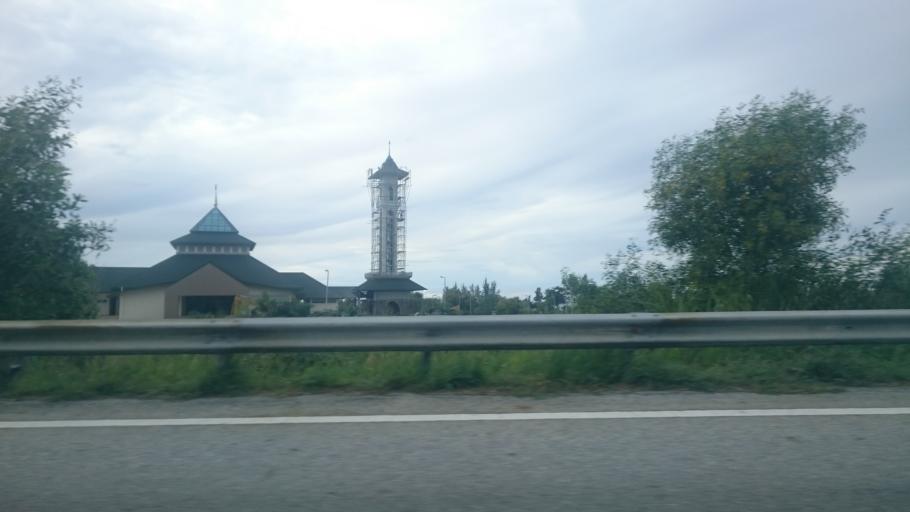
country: BN
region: Tutong
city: Tutong
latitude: 4.8133
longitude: 114.6506
